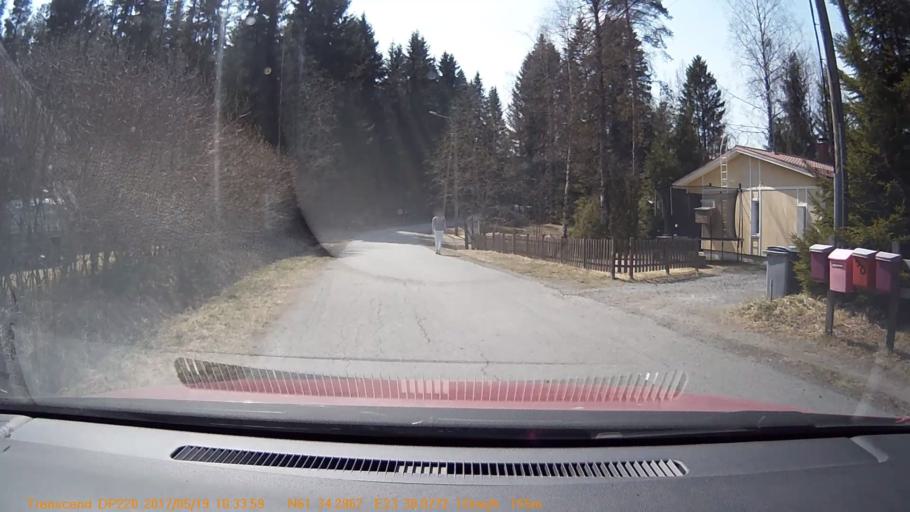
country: FI
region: Pirkanmaa
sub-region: Tampere
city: Yloejaervi
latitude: 61.5716
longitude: 23.5013
